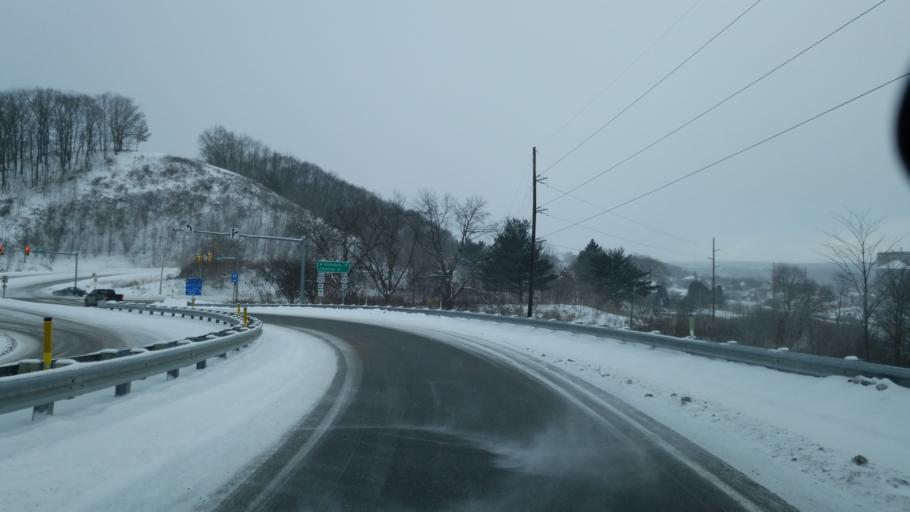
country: US
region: Pennsylvania
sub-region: Clearfield County
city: Clearfield
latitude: 41.0250
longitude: -78.4165
